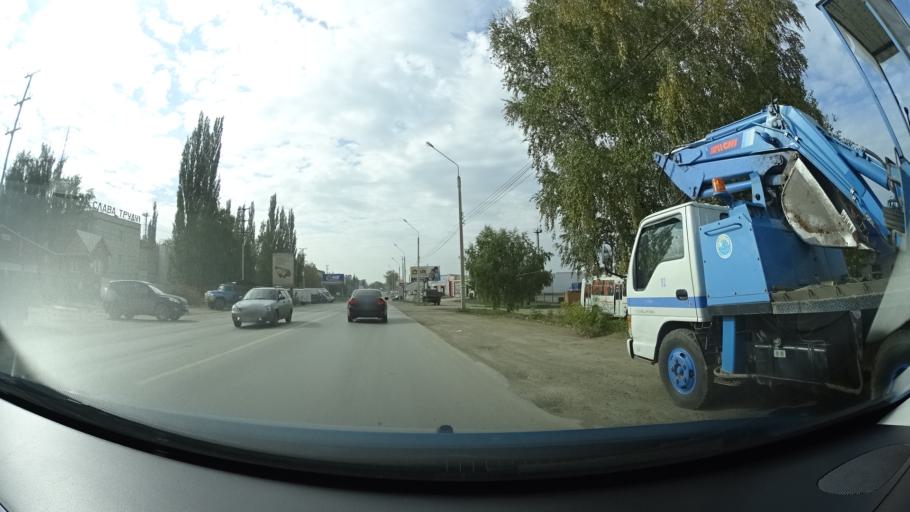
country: RU
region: Bashkortostan
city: Oktyabr'skiy
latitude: 54.4924
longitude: 53.4761
